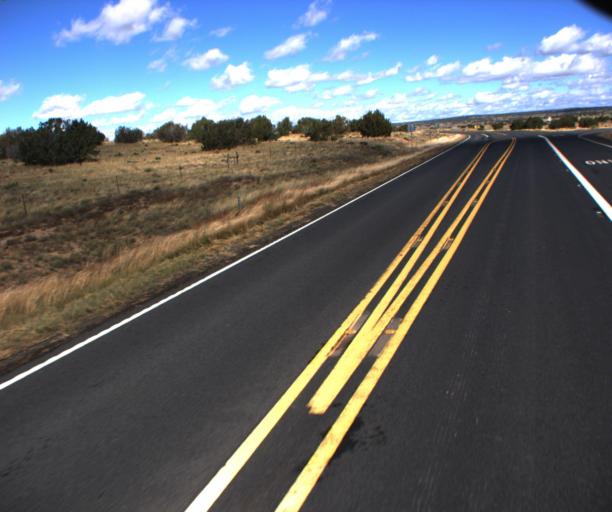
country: US
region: Arizona
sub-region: Apache County
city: Houck
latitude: 34.9991
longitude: -109.2273
